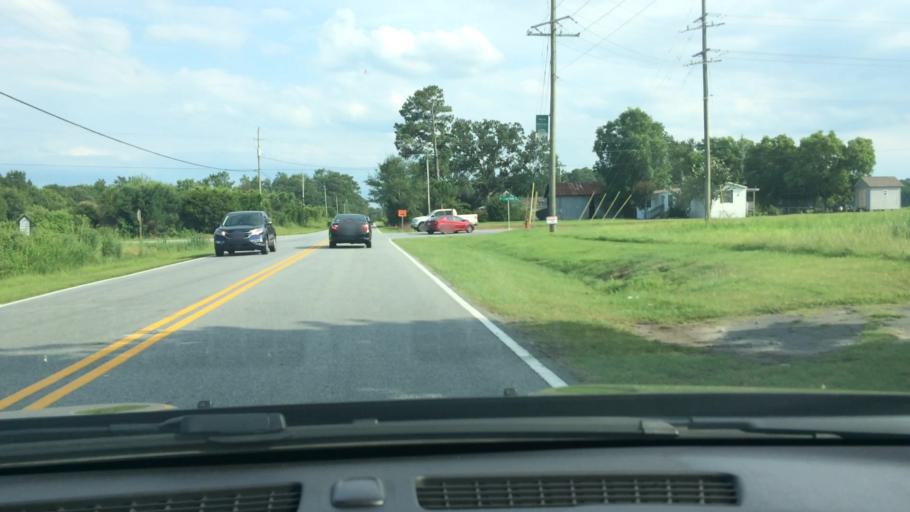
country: US
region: North Carolina
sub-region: Pitt County
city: Winterville
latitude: 35.5183
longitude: -77.3842
